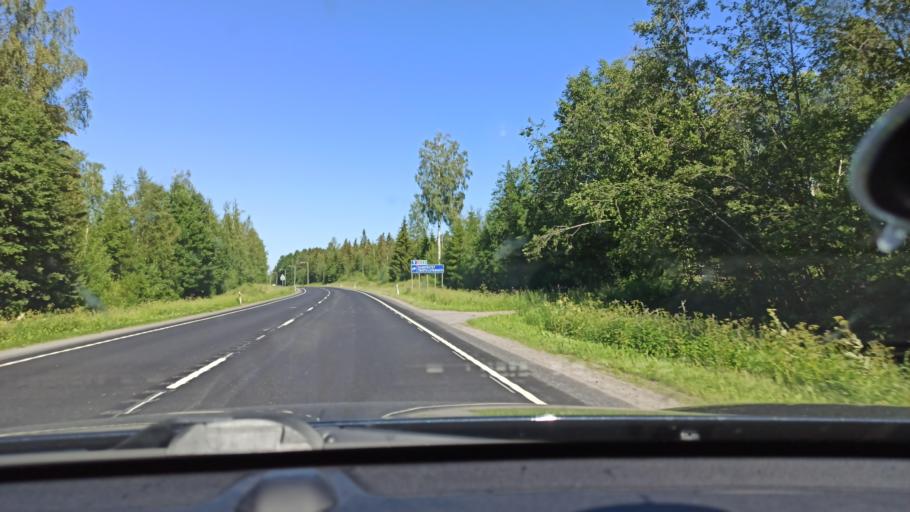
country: FI
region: Ostrobothnia
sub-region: Vaasa
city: Oravais
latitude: 63.2804
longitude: 22.3498
